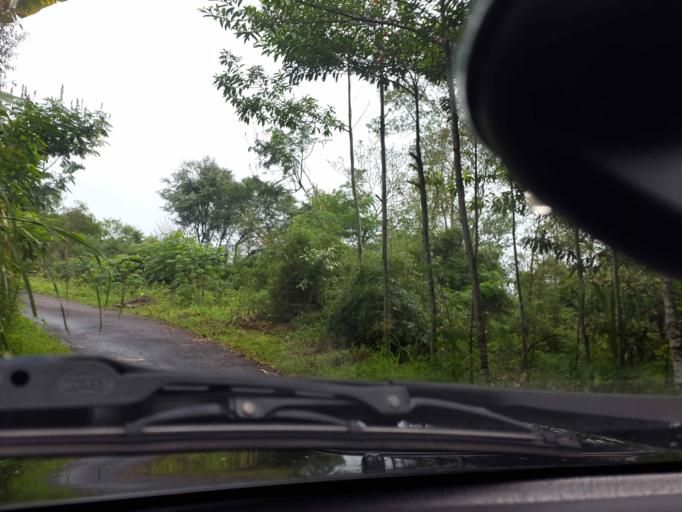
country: ID
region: Central Java
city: Wonosobo
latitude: -7.3940
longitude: 110.0198
